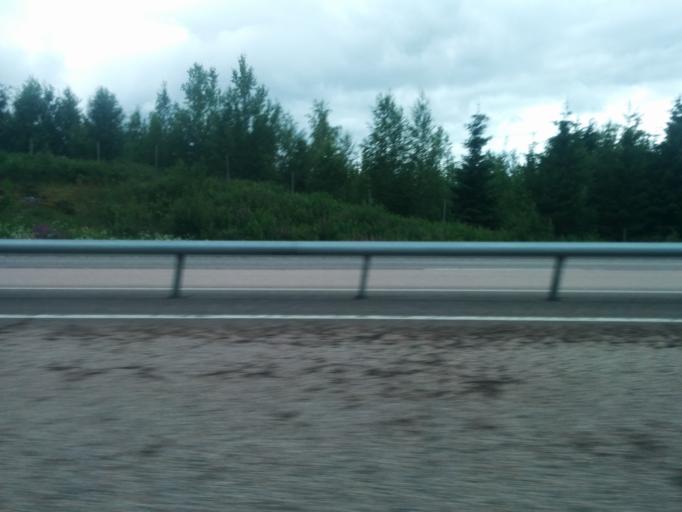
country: FI
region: Pirkanmaa
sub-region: Tampere
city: Orivesi
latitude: 61.7078
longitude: 24.5400
